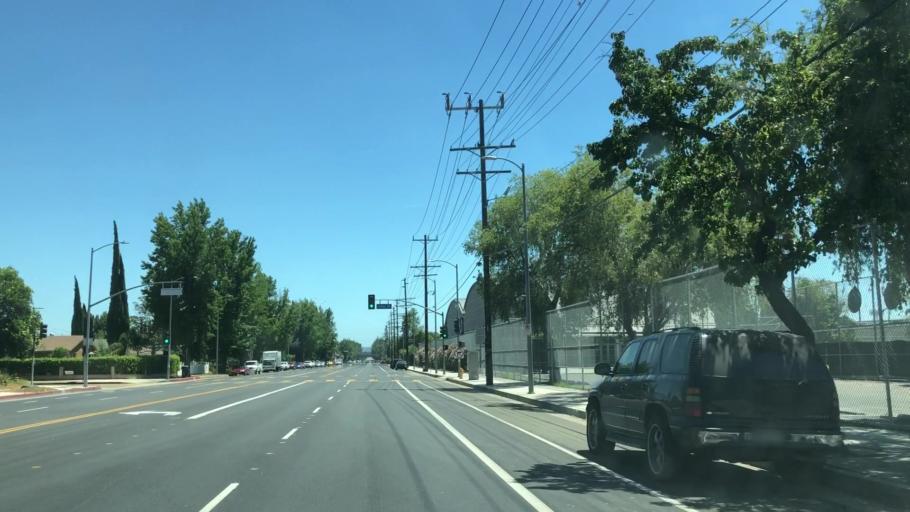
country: US
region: California
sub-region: Los Angeles County
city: San Fernando
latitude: 34.2762
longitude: -118.4847
